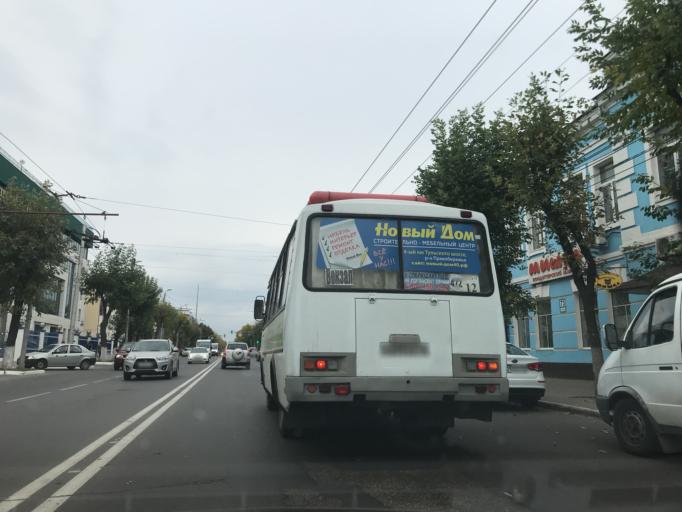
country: RU
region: Kaluga
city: Kaluga
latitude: 54.5141
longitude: 36.2642
